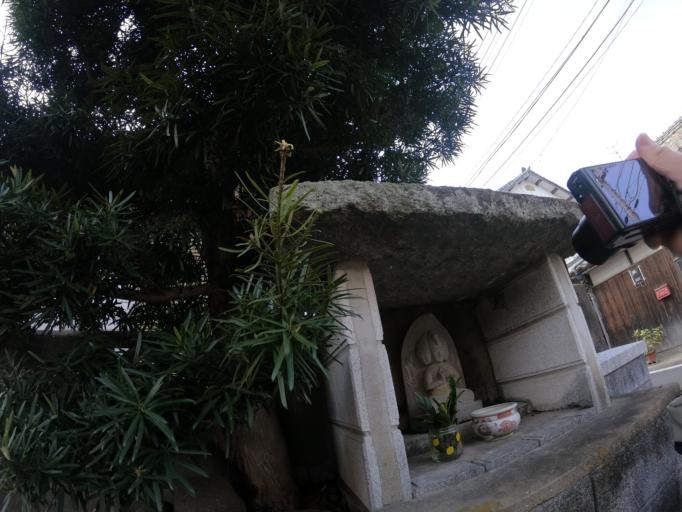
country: JP
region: Nagasaki
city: Shimabara
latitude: 32.6675
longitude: 130.3068
